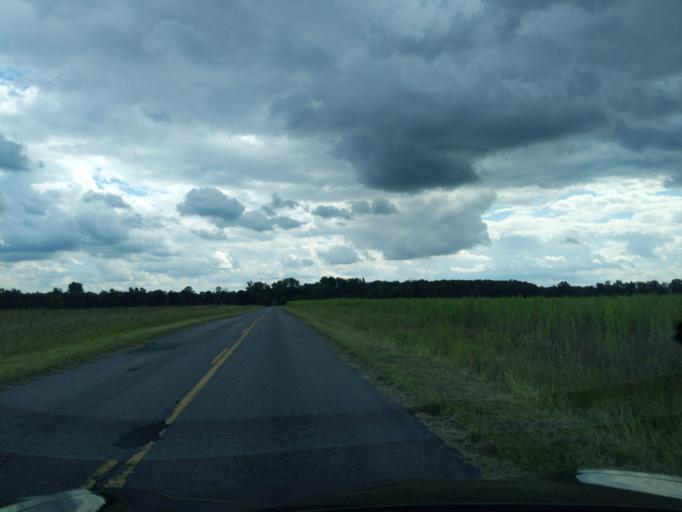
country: US
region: Michigan
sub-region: Eaton County
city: Eaton Rapids
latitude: 42.4408
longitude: -84.5803
